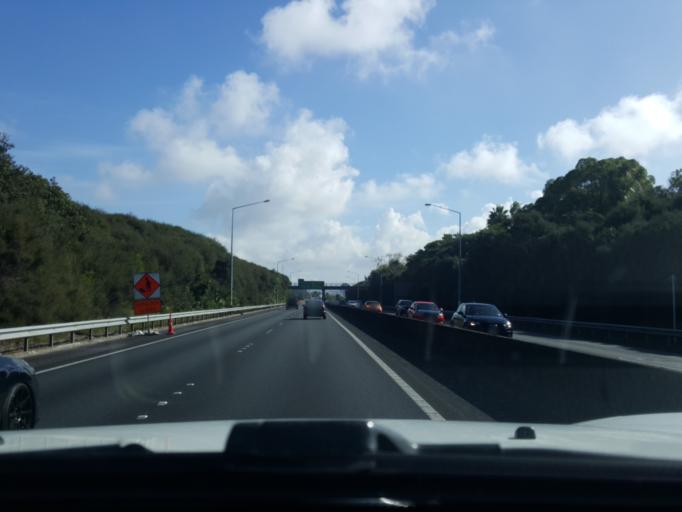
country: NZ
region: Auckland
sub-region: Auckland
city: Mangere
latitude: -36.9692
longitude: 174.8095
